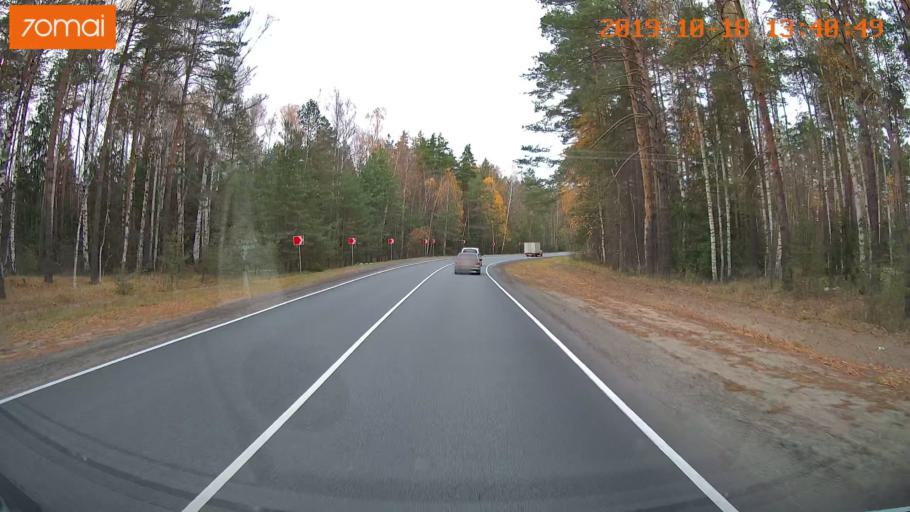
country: RU
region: Rjazan
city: Solotcha
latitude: 54.9143
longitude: 39.9977
